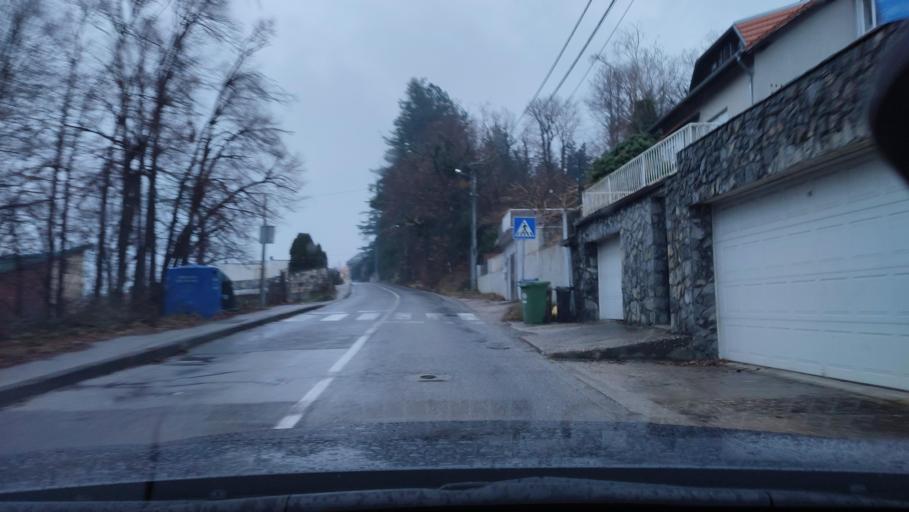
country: HR
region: Grad Zagreb
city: Zagreb
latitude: 45.8488
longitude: 15.9536
